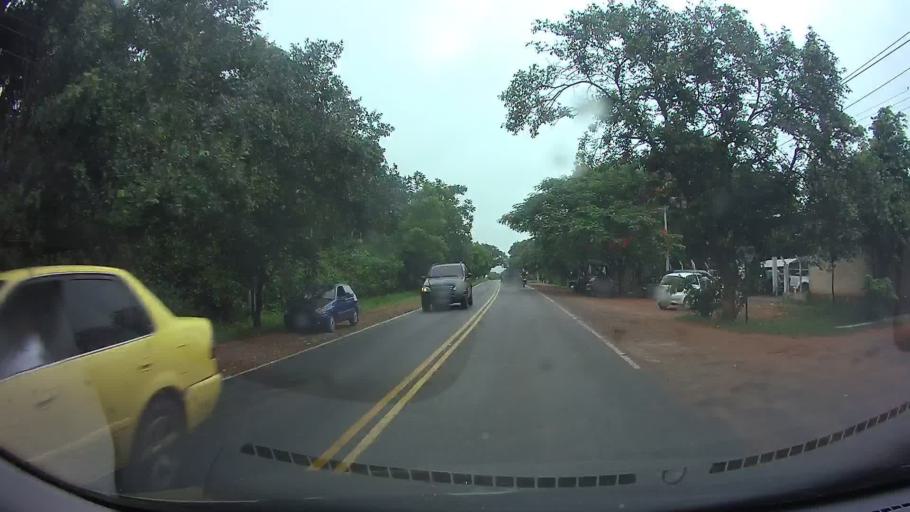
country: PY
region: Central
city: Itaugua
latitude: -25.4040
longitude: -57.3587
